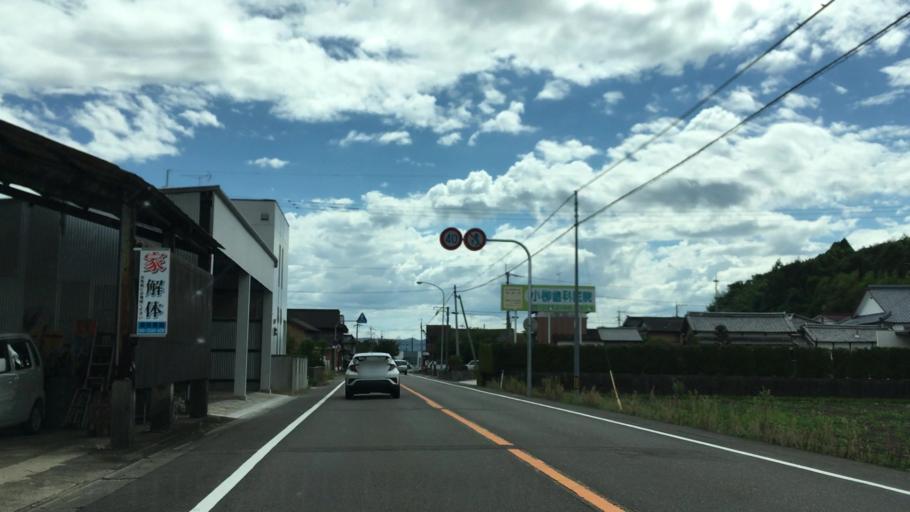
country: JP
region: Saga Prefecture
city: Saga-shi
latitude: 33.2219
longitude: 130.1714
